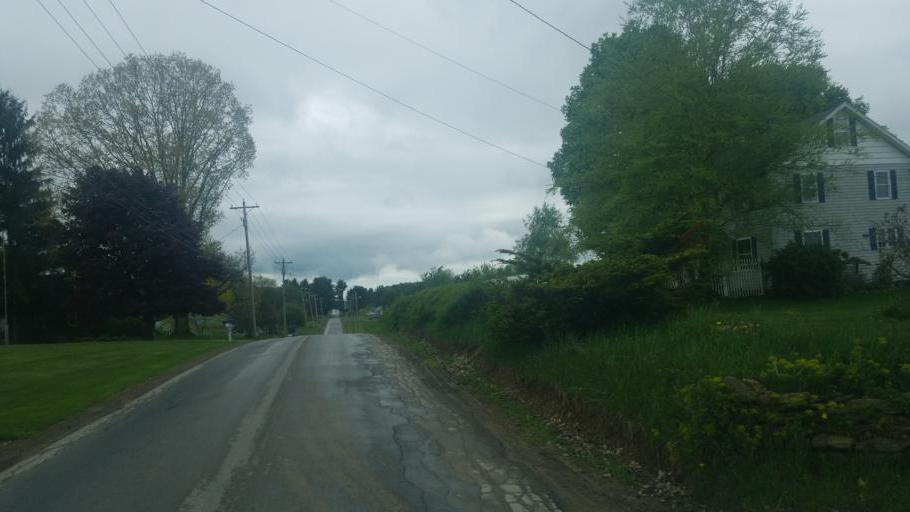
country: US
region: Pennsylvania
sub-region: Forest County
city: Tionesta
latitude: 41.4004
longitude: -79.3880
